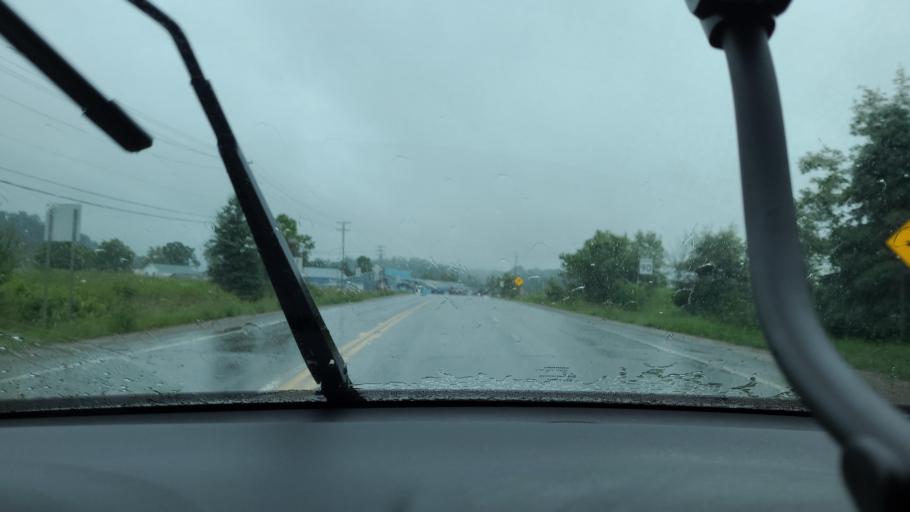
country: CA
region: Quebec
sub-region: Outaouais
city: Saint-Andre-Avellin
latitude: 45.8256
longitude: -75.0671
